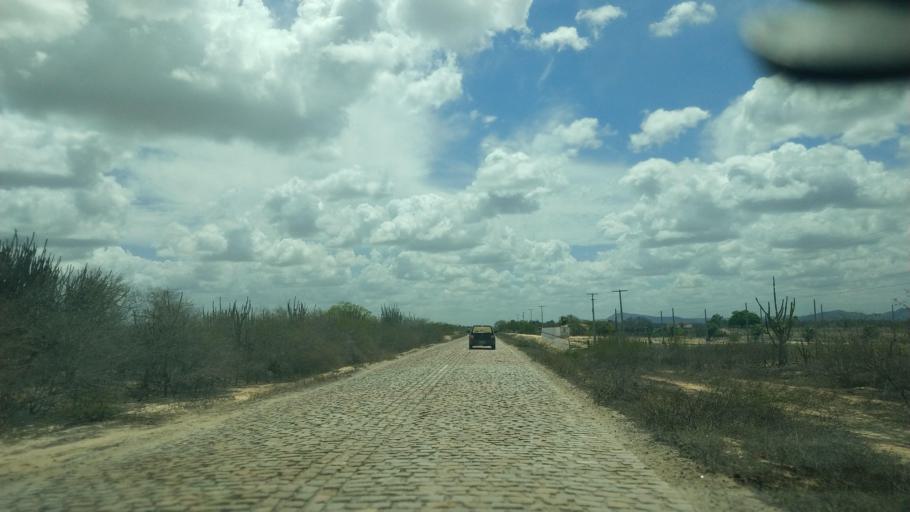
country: BR
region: Rio Grande do Norte
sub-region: Sao Paulo Do Potengi
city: Sao Paulo do Potengi
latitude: -5.9691
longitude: -35.8529
